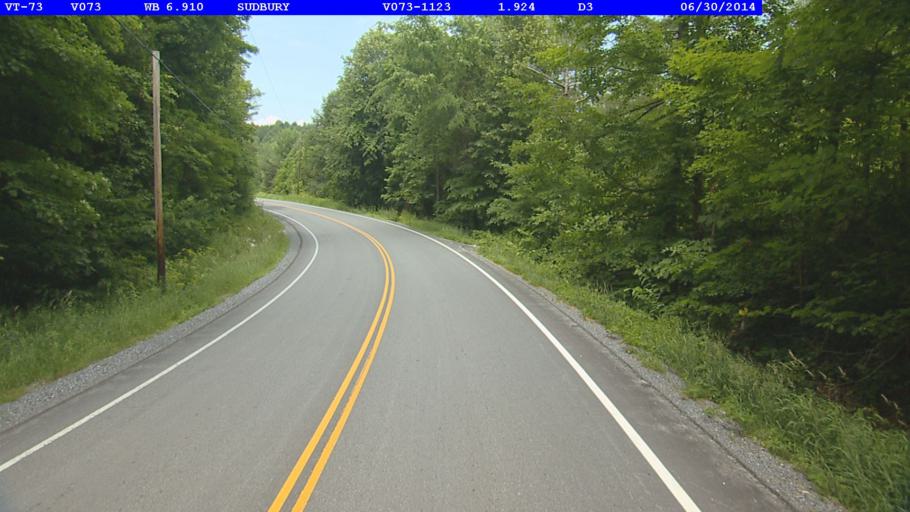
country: US
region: Vermont
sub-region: Rutland County
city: Brandon
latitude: 43.8193
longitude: -73.1640
